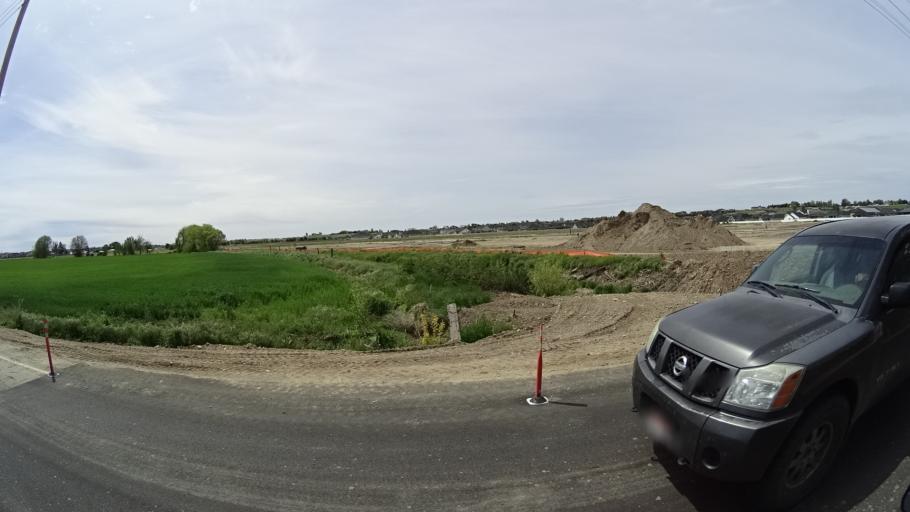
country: US
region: Idaho
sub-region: Ada County
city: Meridian
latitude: 43.5614
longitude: -116.3615
